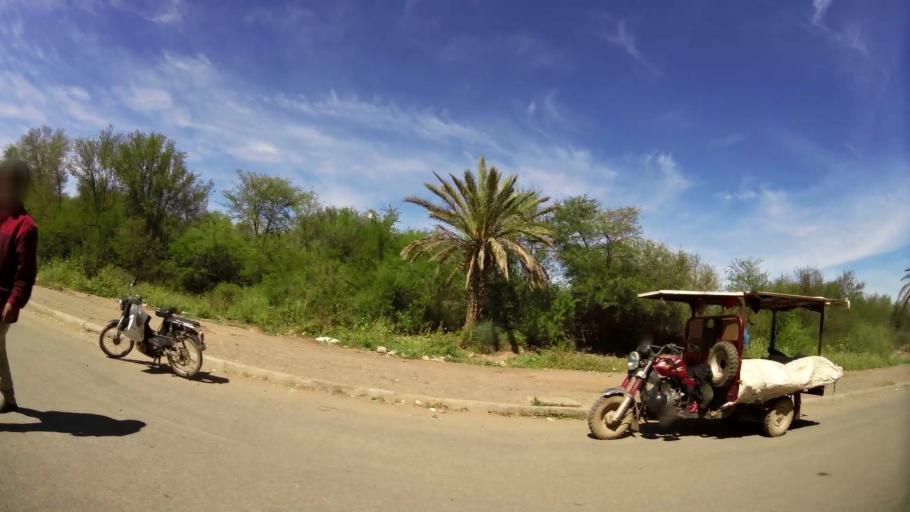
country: MA
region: Marrakech-Tensift-Al Haouz
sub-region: Marrakech
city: Marrakesh
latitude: 31.6437
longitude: -8.1103
